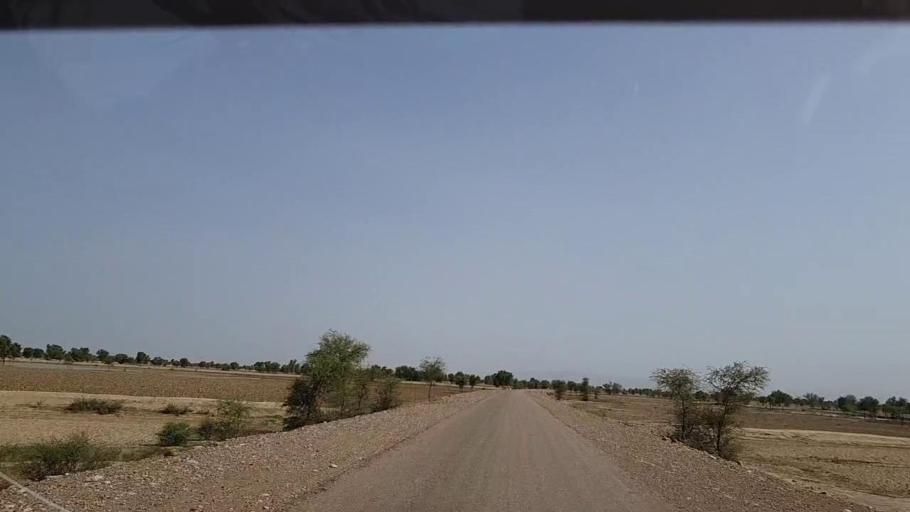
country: PK
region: Sindh
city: Johi
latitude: 26.6507
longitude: 67.5047
